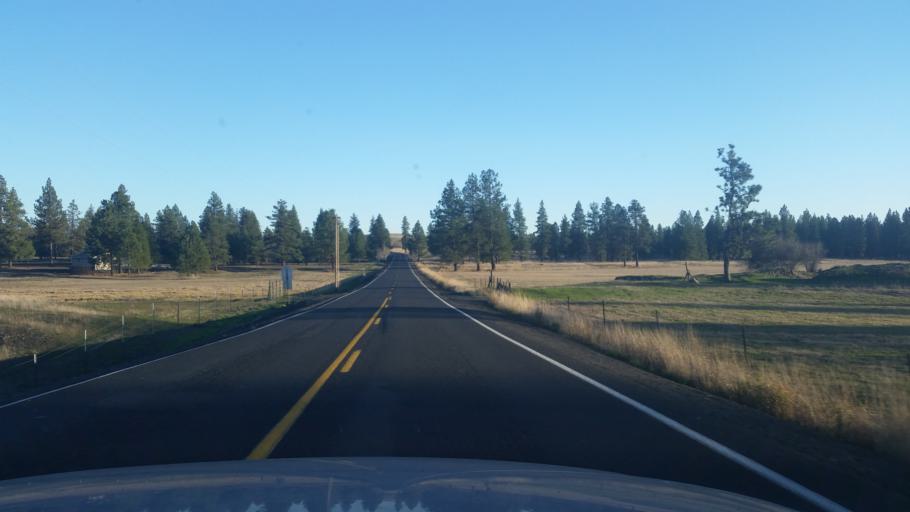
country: US
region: Washington
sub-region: Spokane County
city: Opportunity
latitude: 47.3828
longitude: -117.3152
